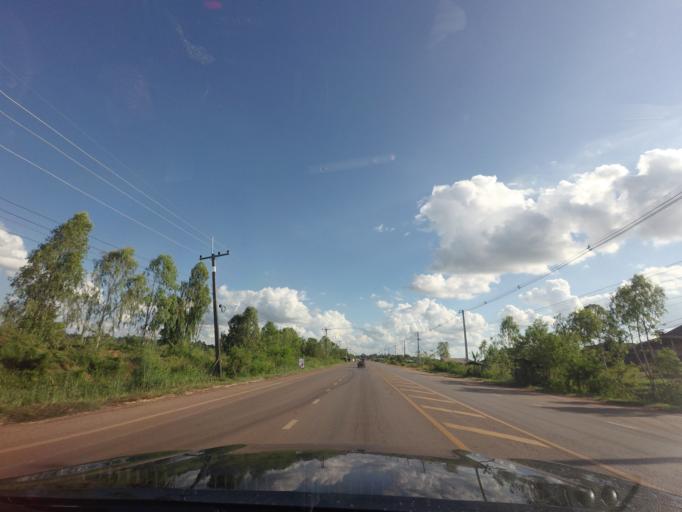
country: TH
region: Changwat Udon Thani
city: Ban Dung
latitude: 17.7166
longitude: 103.2502
